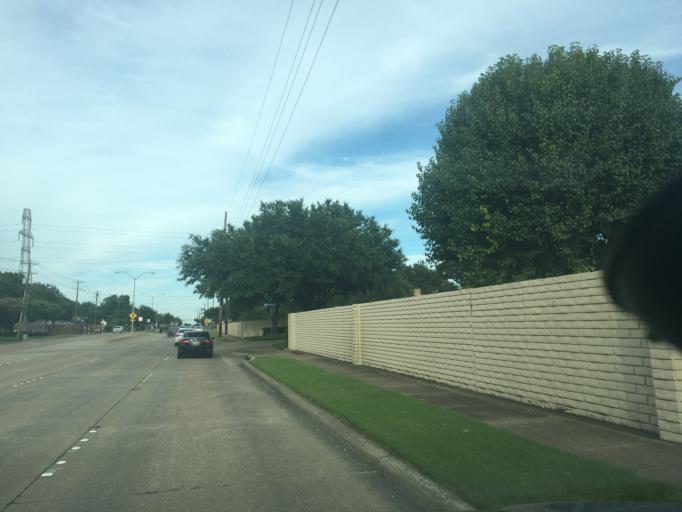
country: US
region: Texas
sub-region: Dallas County
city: Richardson
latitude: 32.9605
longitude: -96.6970
